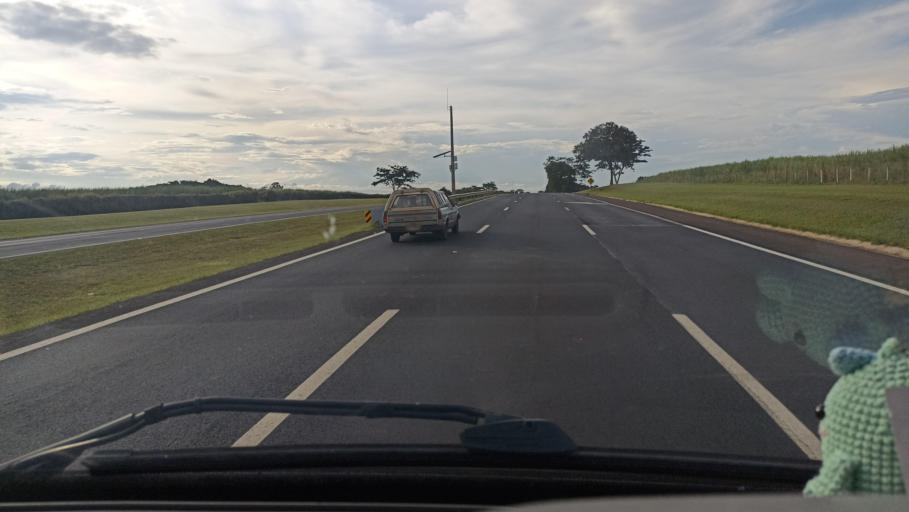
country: BR
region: Sao Paulo
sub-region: Bebedouro
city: Bebedouro
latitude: -20.9884
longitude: -48.4332
